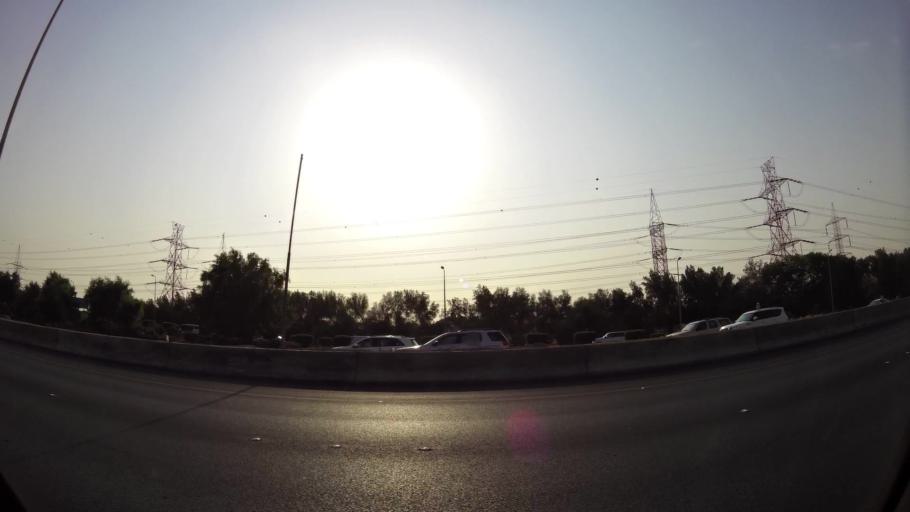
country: KW
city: Bayan
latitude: 29.2820
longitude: 48.0340
